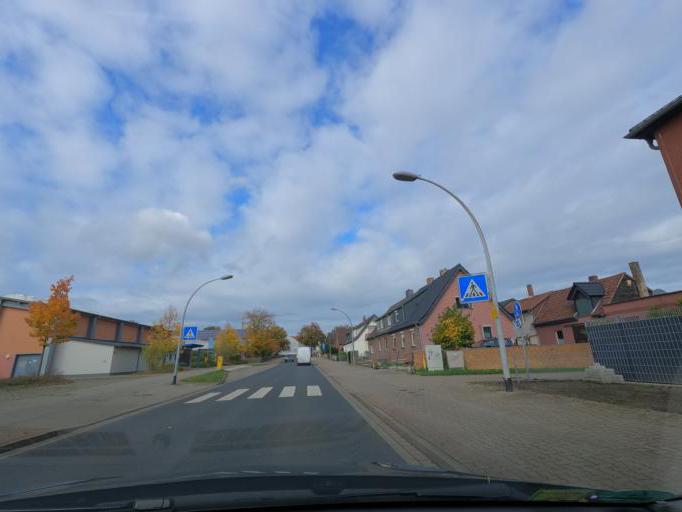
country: DE
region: Lower Saxony
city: Leiferde
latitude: 52.1911
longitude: 10.4792
